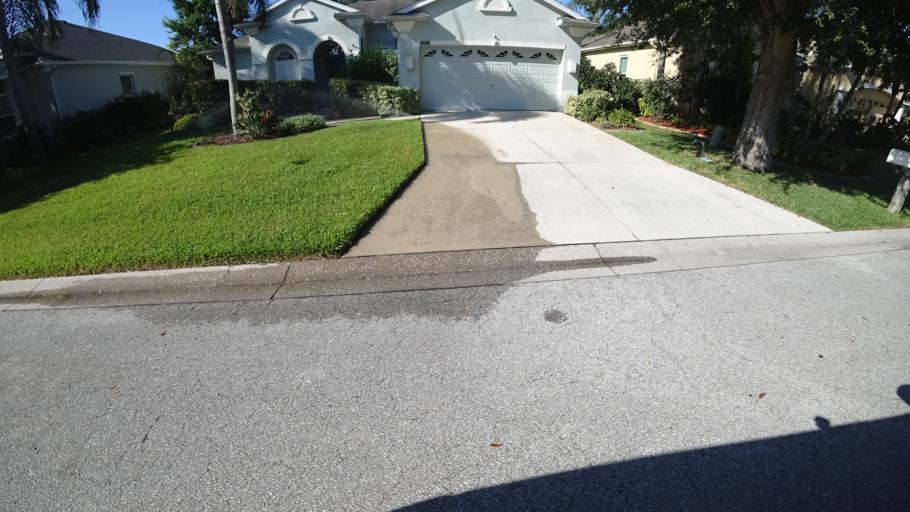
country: US
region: Florida
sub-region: Manatee County
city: Ellenton
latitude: 27.5047
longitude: -82.5152
